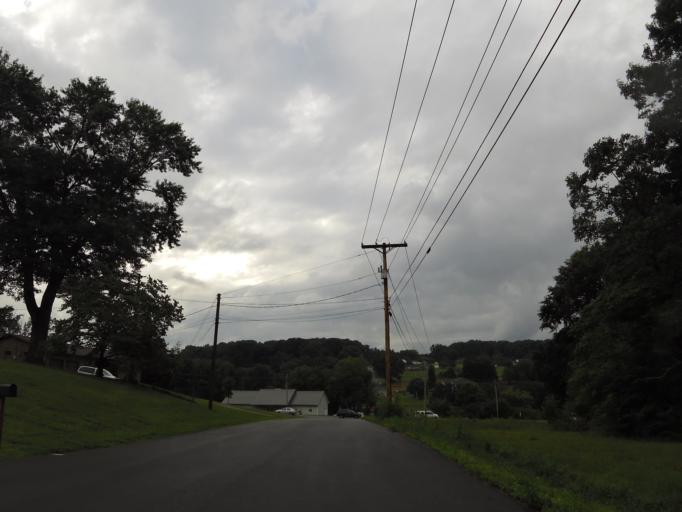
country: US
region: Tennessee
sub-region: Blount County
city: Eagleton Village
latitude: 35.7913
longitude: -83.9133
